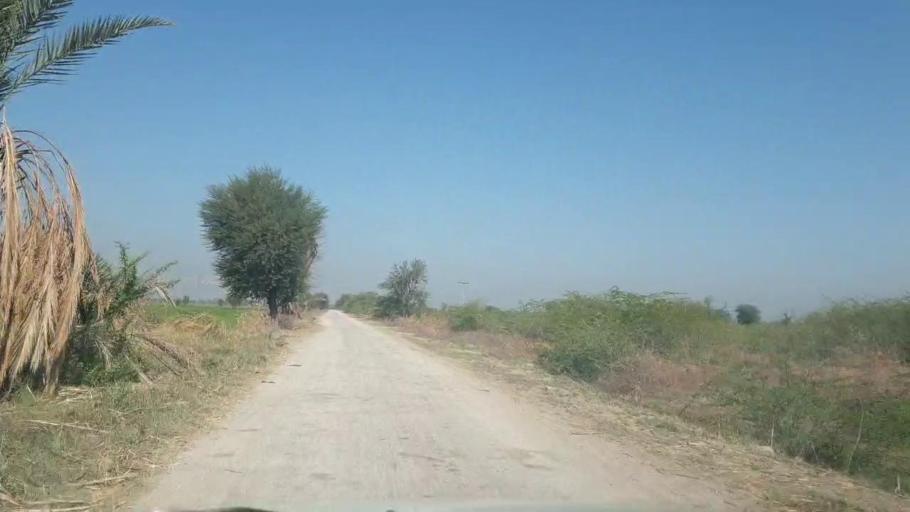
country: PK
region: Sindh
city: Mirpur Khas
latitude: 25.5029
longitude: 69.1729
